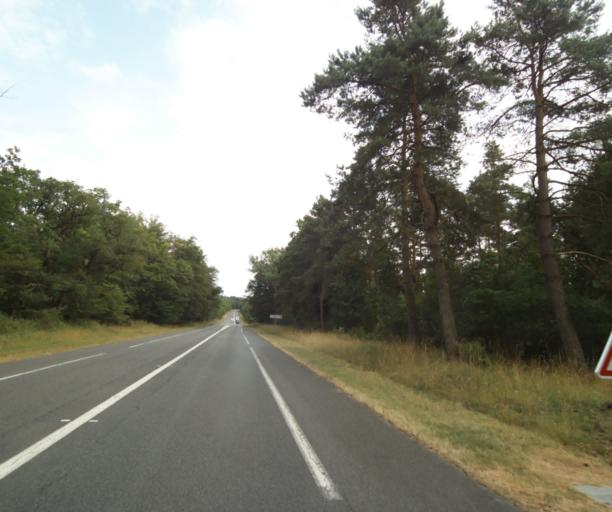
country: FR
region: Ile-de-France
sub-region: Departement de Seine-et-Marne
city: Fontainebleau
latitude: 48.4355
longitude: 2.6946
